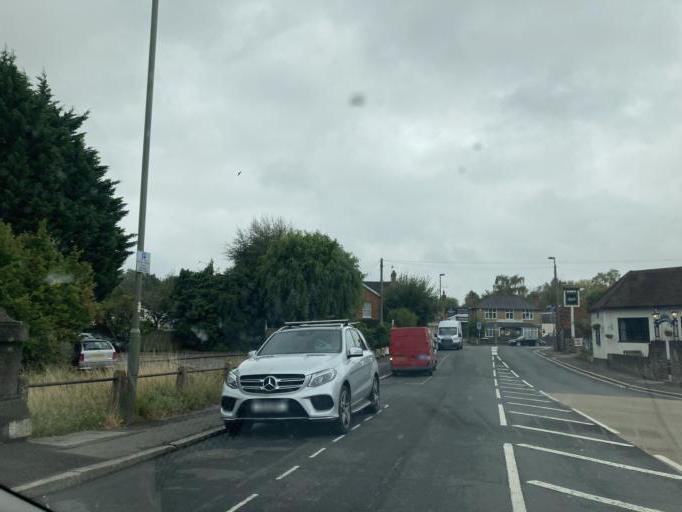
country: GB
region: England
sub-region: Surrey
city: Bagshot
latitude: 51.3623
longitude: -0.6911
